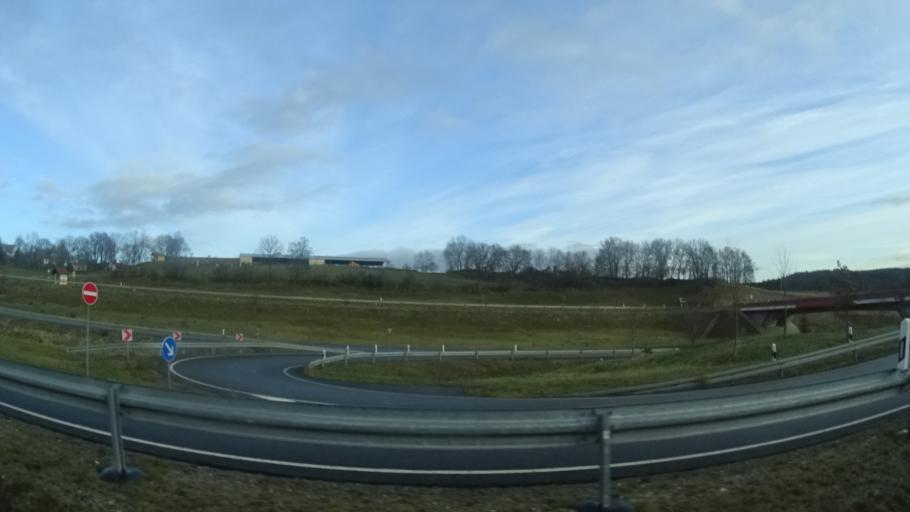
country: DE
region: Thuringia
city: Bad Blankenburg
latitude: 50.7318
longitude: 11.2466
